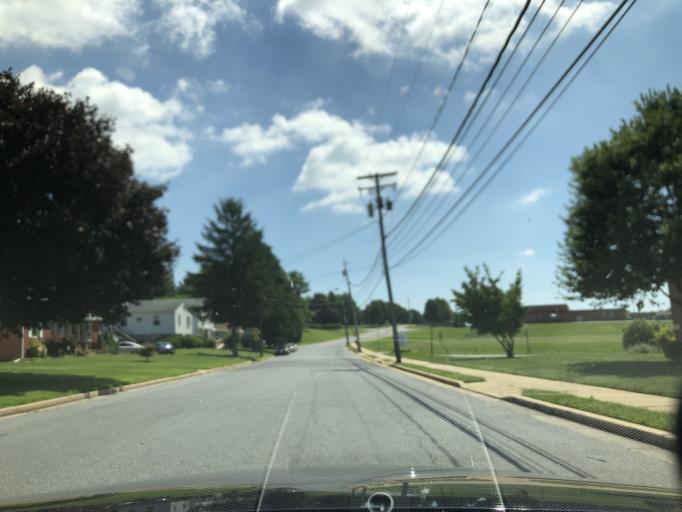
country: US
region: Maryland
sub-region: Carroll County
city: Westminster
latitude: 39.5842
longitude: -76.9973
